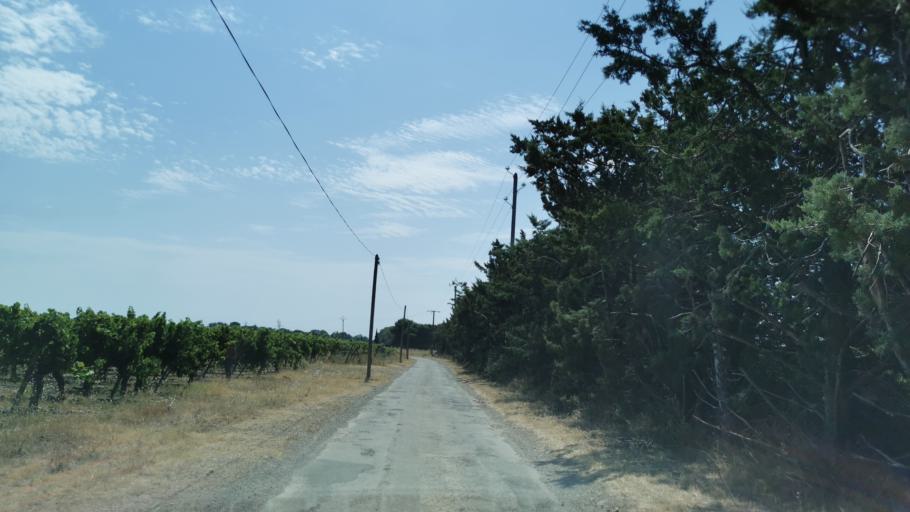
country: FR
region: Languedoc-Roussillon
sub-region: Departement de l'Aude
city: Argeliers
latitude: 43.2901
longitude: 2.8910
